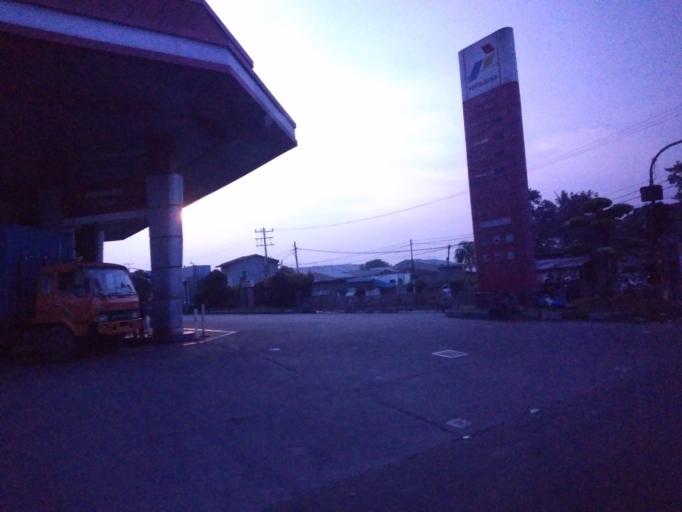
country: ID
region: North Sumatra
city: Medan
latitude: 3.6393
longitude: 98.6812
